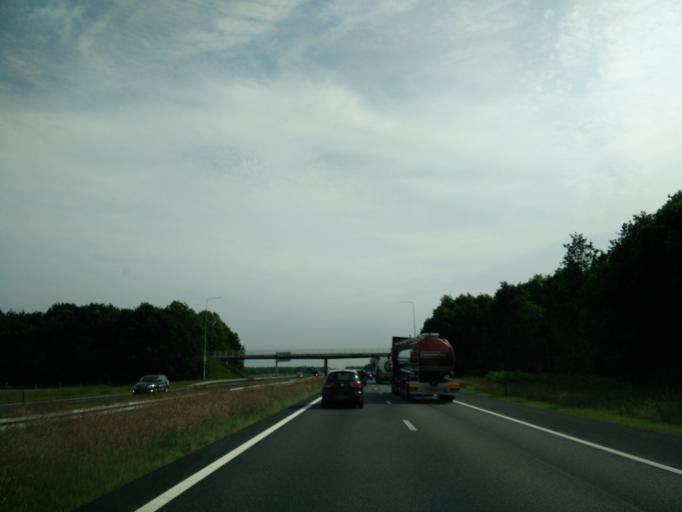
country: NL
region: Drenthe
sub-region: Gemeente Assen
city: Assen
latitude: 52.9453
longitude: 6.5399
